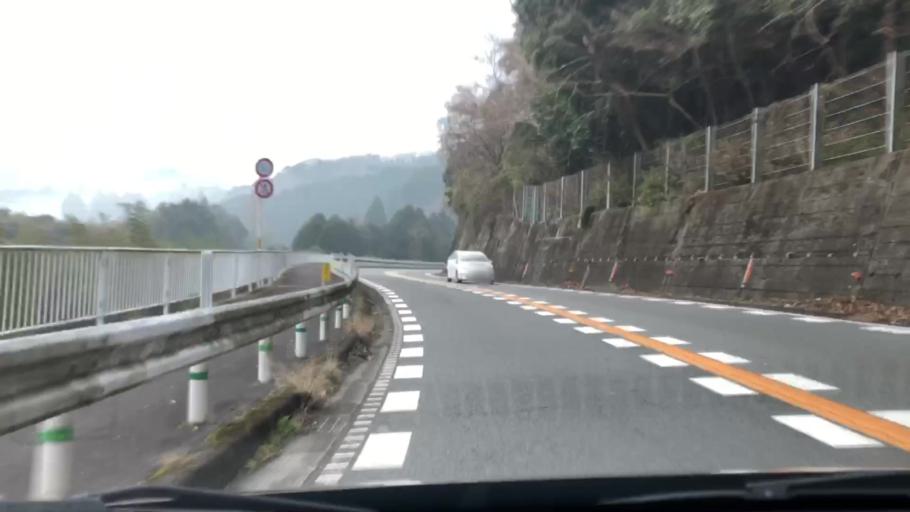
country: JP
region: Oita
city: Usuki
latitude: 33.0267
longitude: 131.6946
